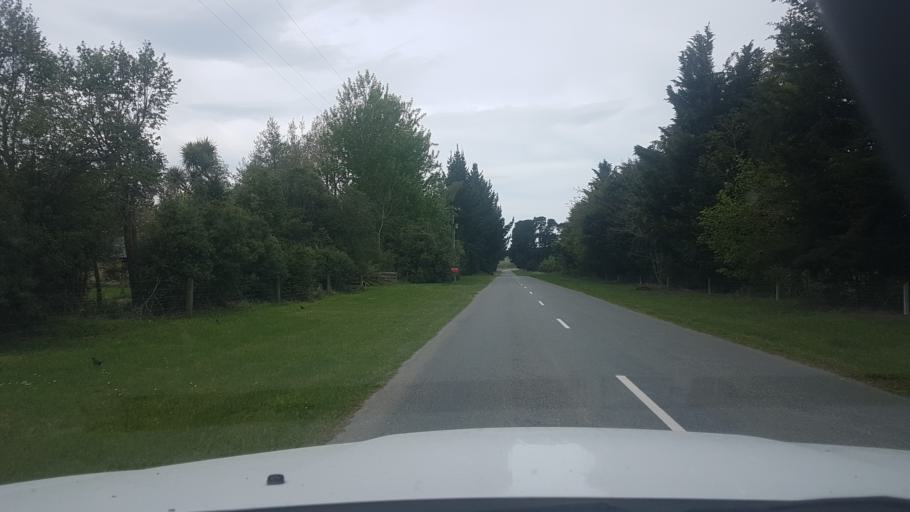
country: NZ
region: Canterbury
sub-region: Timaru District
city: Pleasant Point
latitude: -44.0721
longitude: 171.1581
